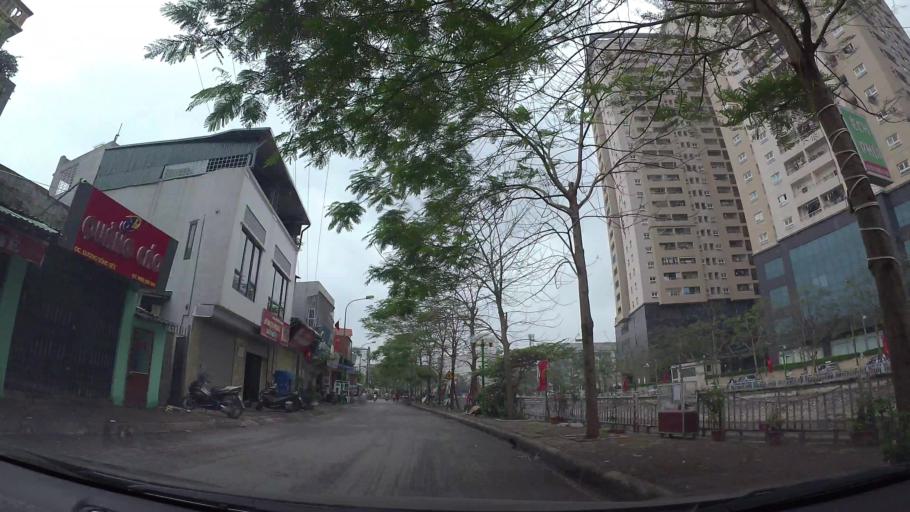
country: VN
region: Ha Noi
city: Hai BaTrung
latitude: 20.9800
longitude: 105.8458
